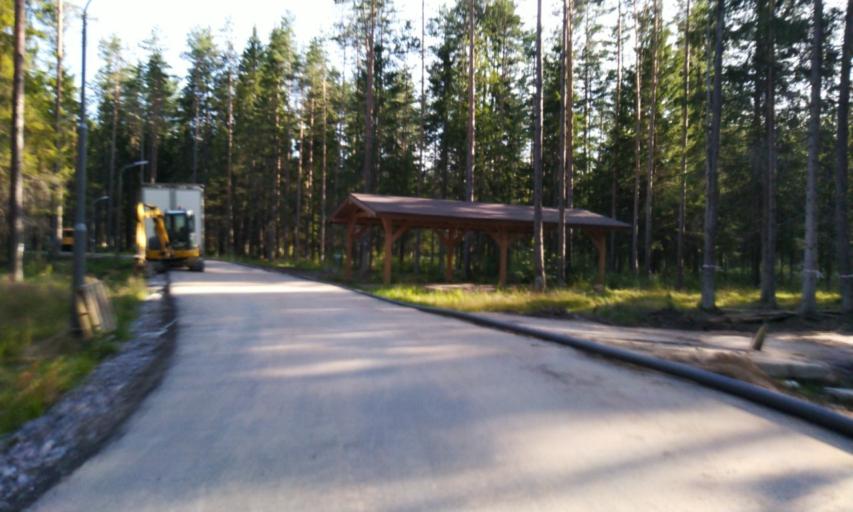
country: RU
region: Leningrad
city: Toksovo
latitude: 60.1328
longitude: 30.4571
